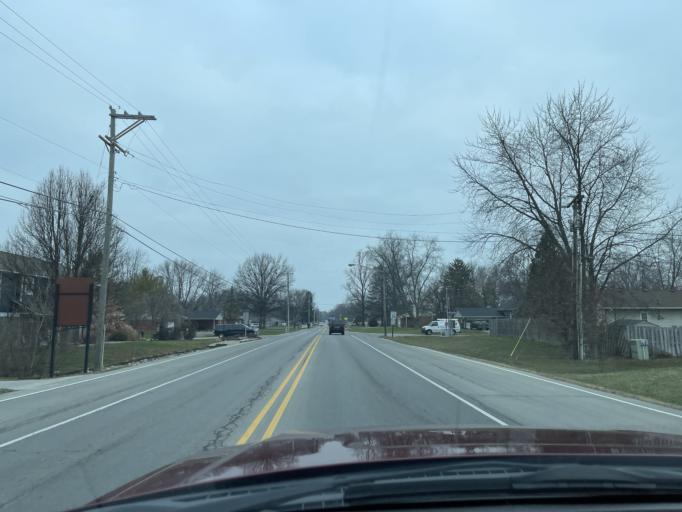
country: US
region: Indiana
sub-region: Hendricks County
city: Brownsburg
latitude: 39.8284
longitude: -86.4012
